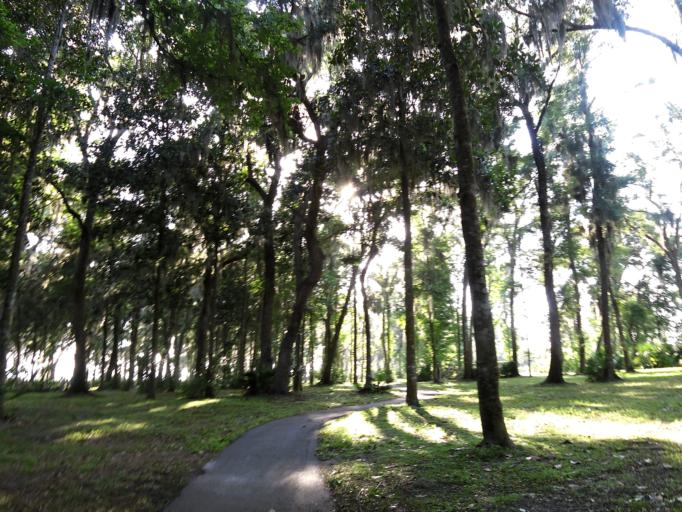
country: US
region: Florida
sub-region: Clay County
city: Green Cove Springs
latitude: 30.0195
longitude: -81.6382
